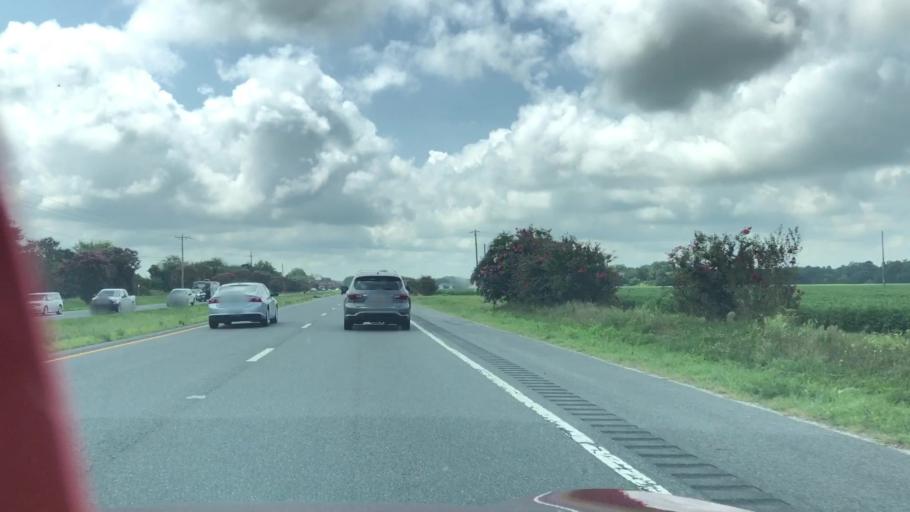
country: US
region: Virginia
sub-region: Northampton County
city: Eastville
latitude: 37.4138
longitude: -75.8982
